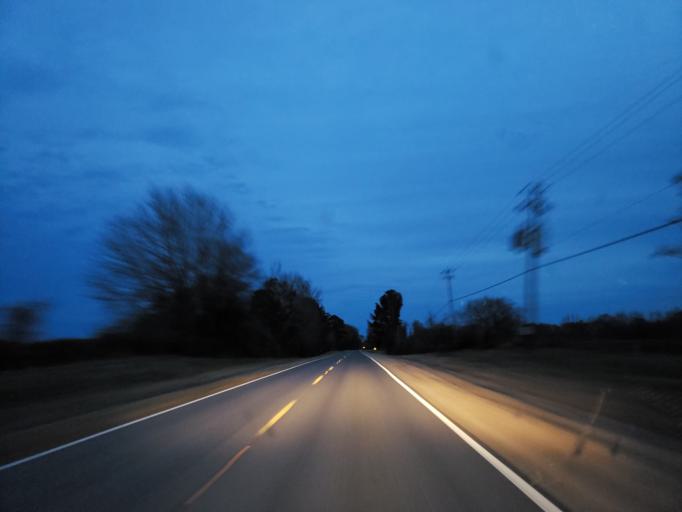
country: US
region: Alabama
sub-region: Greene County
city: Eutaw
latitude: 32.8901
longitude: -87.9478
